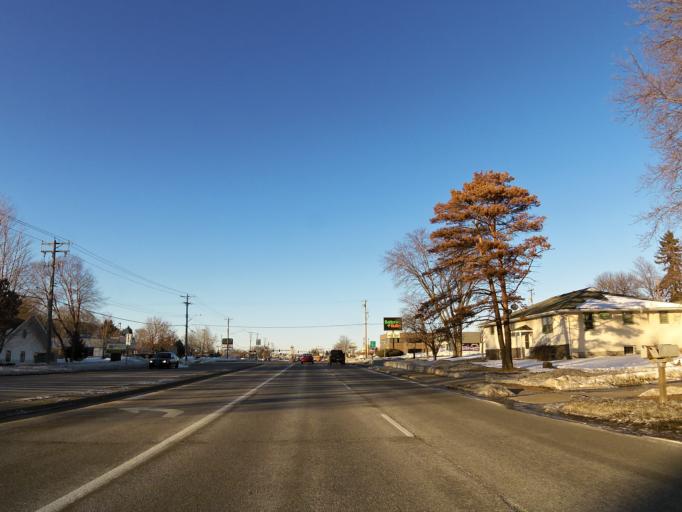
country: US
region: Minnesota
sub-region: Ramsey County
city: North Saint Paul
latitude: 45.0255
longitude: -93.0180
